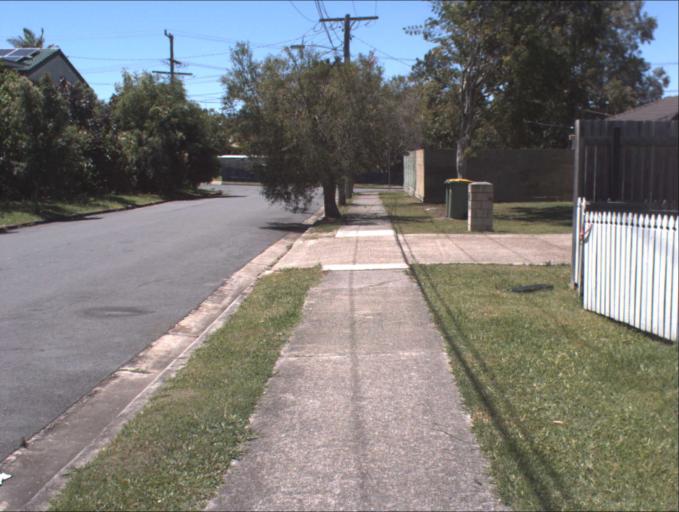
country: AU
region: Queensland
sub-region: Logan
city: Logan City
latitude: -27.6430
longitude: 153.1206
